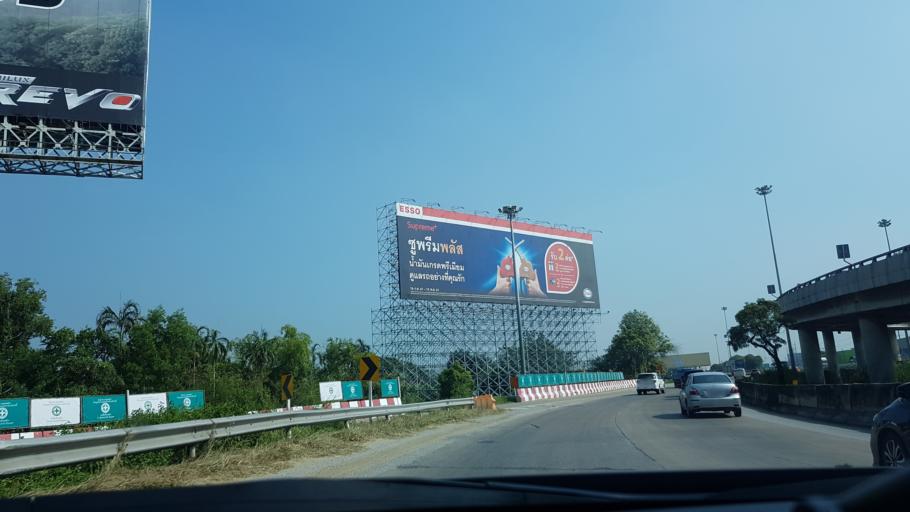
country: TH
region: Phra Nakhon Si Ayutthaya
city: Bang Pa-in
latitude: 14.1775
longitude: 100.6177
